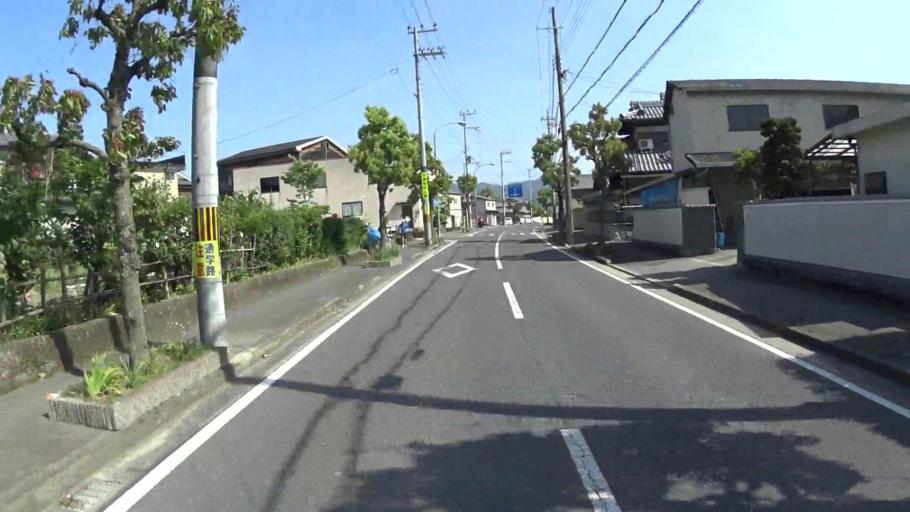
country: JP
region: Kyoto
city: Kameoka
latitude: 35.0237
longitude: 135.5887
